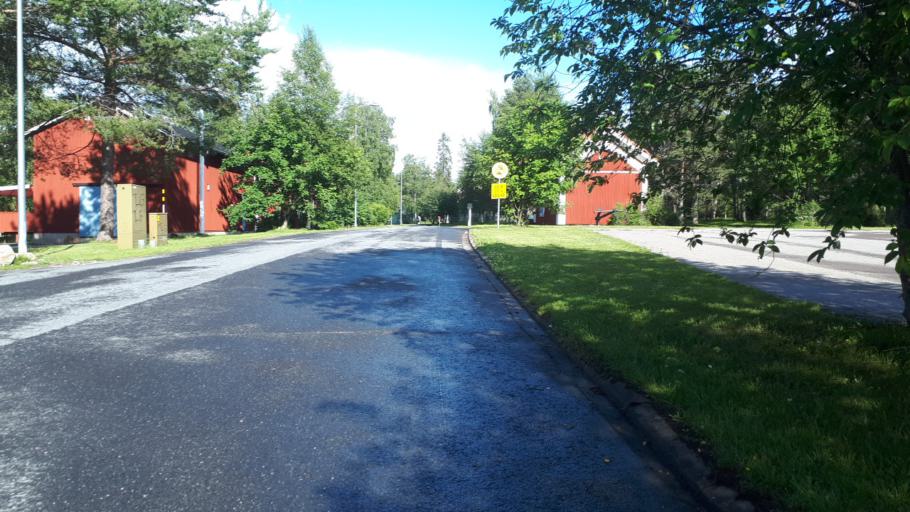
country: FI
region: Northern Ostrobothnia
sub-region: Oulunkaari
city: Ii
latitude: 65.3237
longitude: 25.3675
